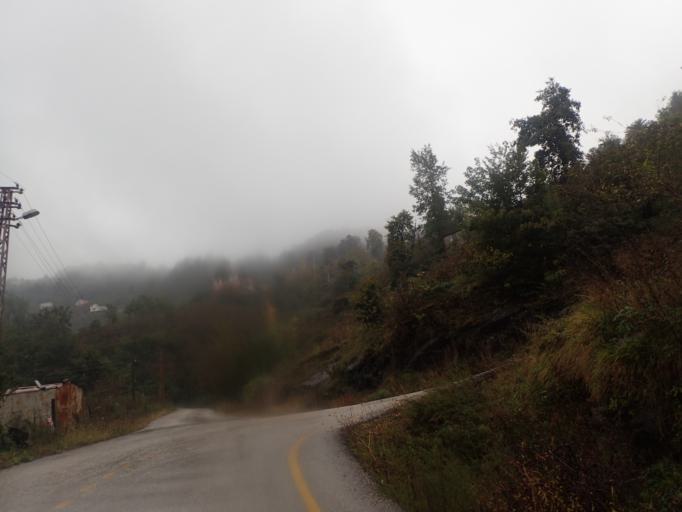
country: TR
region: Ordu
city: Persembe
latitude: 41.0428
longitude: 37.7294
